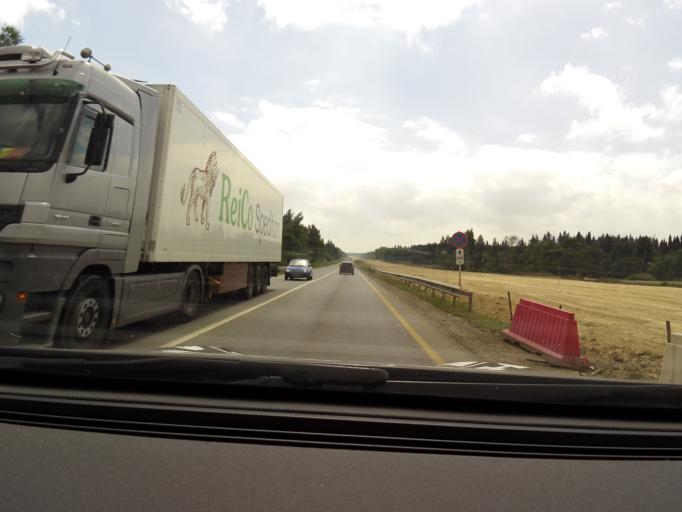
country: RU
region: Perm
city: Kukushtan
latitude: 57.6723
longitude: 56.4350
